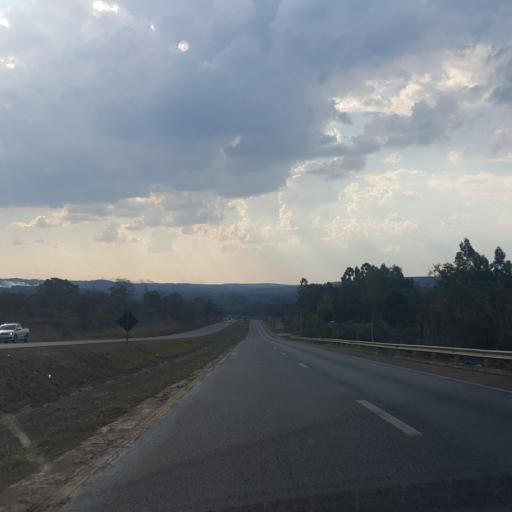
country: BR
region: Goias
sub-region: Abadiania
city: Abadiania
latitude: -16.1078
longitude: -48.4493
